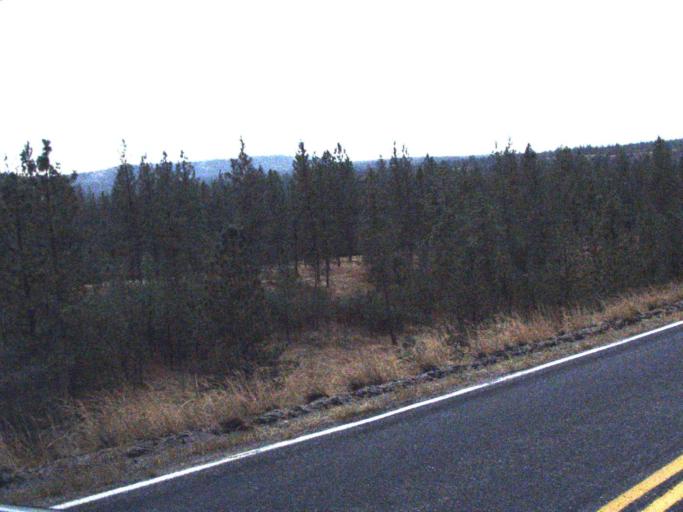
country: US
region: Washington
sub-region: Spokane County
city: Fairchild Air Force Base
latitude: 47.8502
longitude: -117.8527
